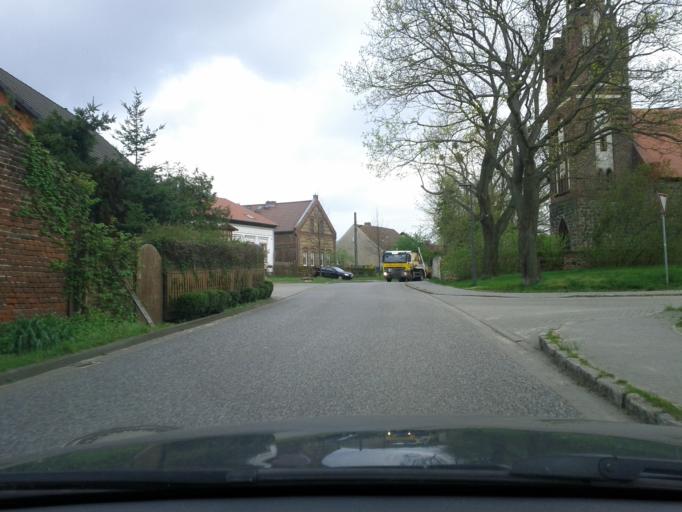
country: DE
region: Brandenburg
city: Hoppegarten
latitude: 52.4911
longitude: 13.6720
